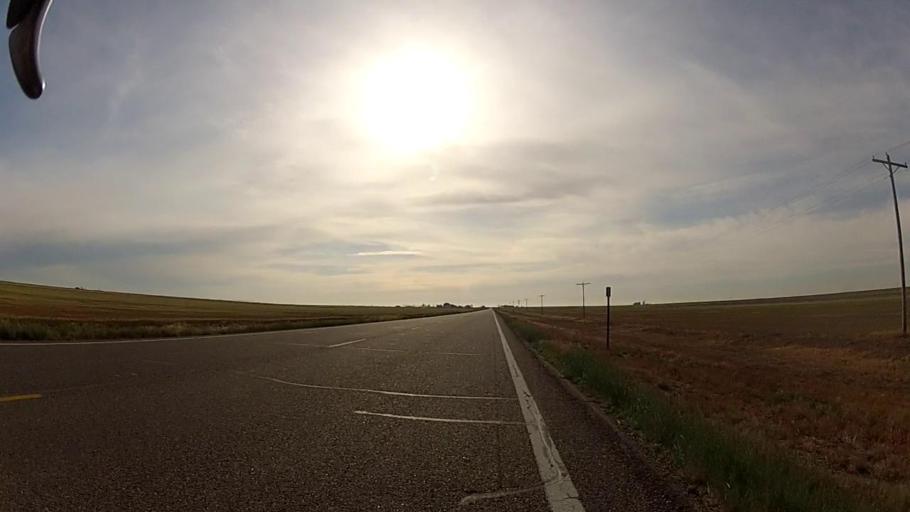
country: US
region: Kansas
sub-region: Grant County
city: Ulysses
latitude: 37.5767
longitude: -101.5028
